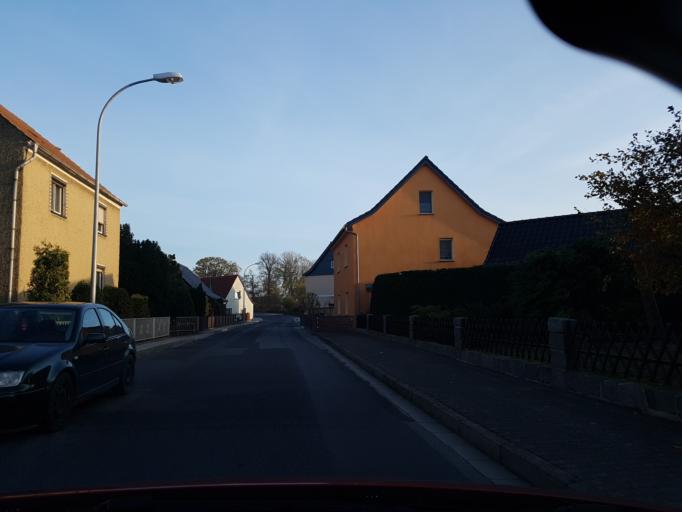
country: DE
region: Saxony
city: Nauwalde
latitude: 51.4410
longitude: 13.4462
